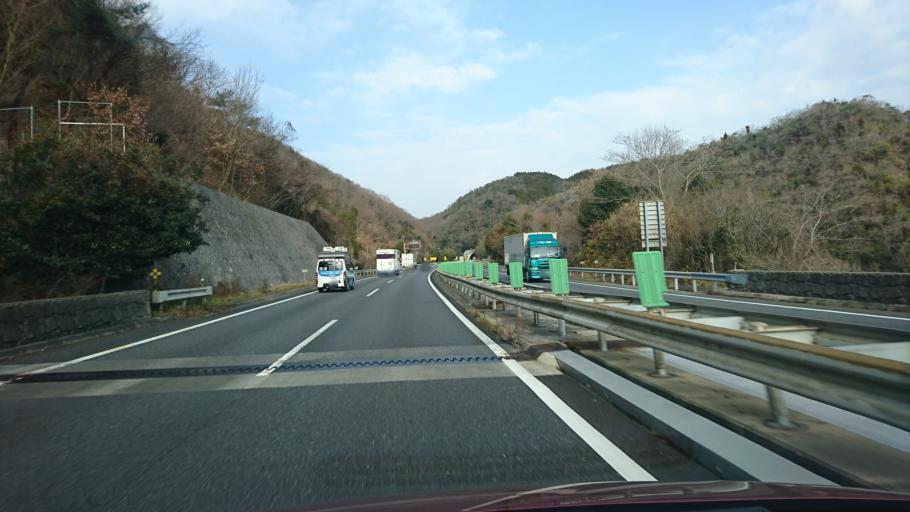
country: JP
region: Hyogo
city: Kariya
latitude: 34.7855
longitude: 134.2173
